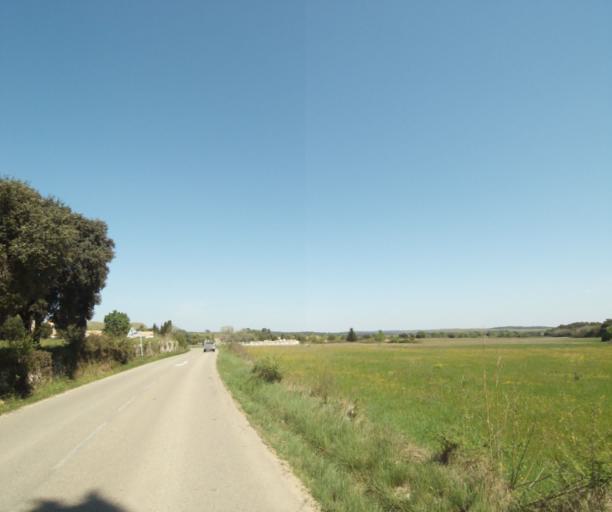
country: FR
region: Languedoc-Roussillon
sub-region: Departement de l'Herault
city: Castries
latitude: 43.6710
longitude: 3.9914
